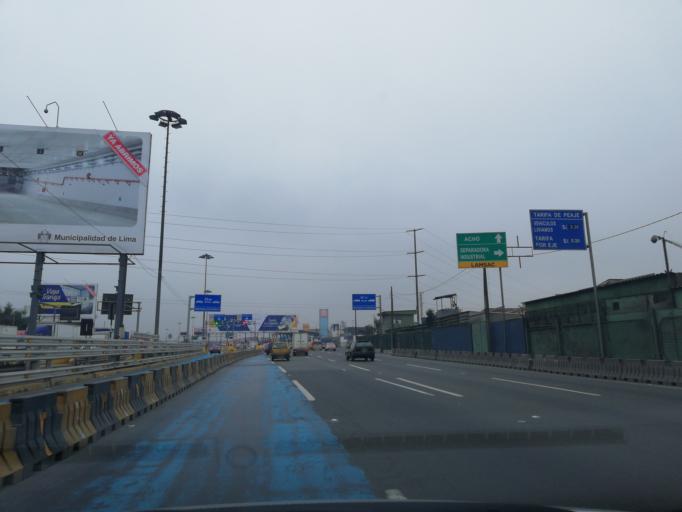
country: PE
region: Lima
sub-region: Lima
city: San Luis
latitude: -12.0689
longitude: -76.9721
